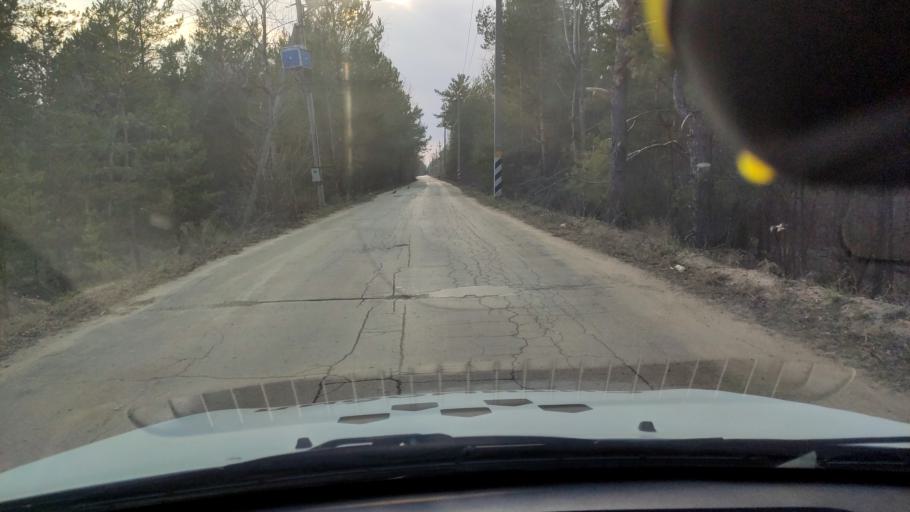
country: RU
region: Samara
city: Zhigulevsk
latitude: 53.4584
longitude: 49.6129
